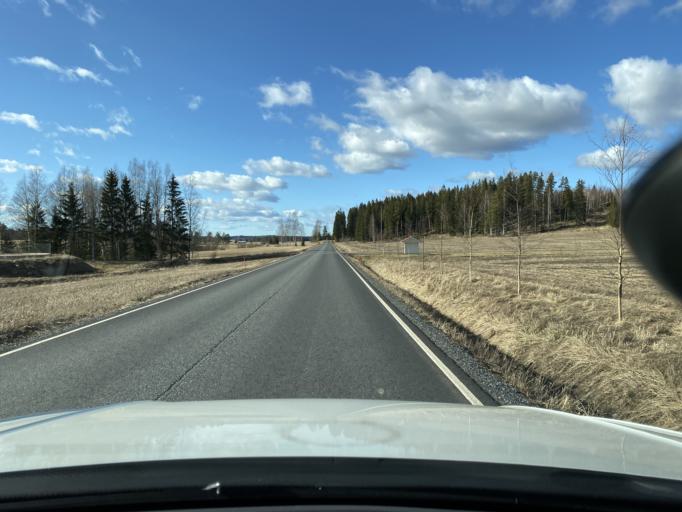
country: FI
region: Pirkanmaa
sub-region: Lounais-Pirkanmaa
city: Punkalaidun
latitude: 61.0804
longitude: 23.2113
